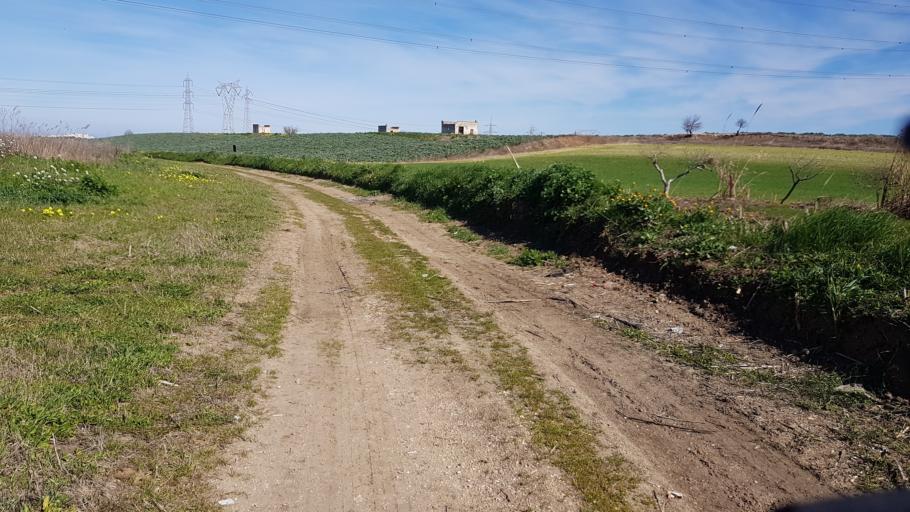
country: IT
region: Apulia
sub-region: Provincia di Brindisi
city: La Rosa
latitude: 40.5958
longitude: 17.9267
